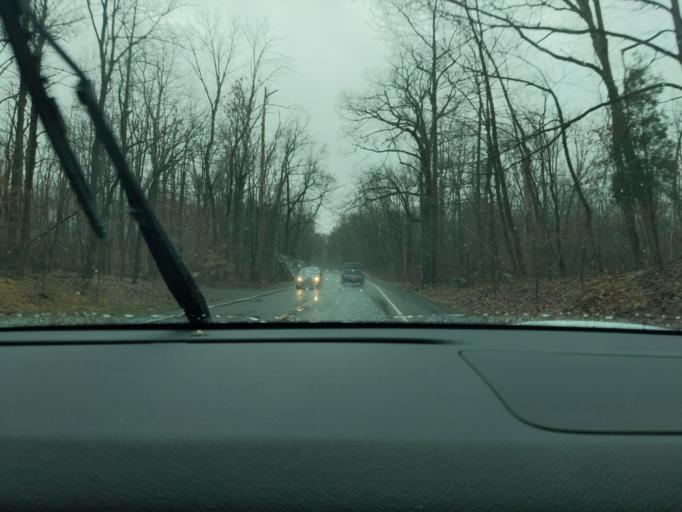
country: US
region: Pennsylvania
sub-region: Bucks County
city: Perkasie
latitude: 40.4238
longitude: -75.2804
